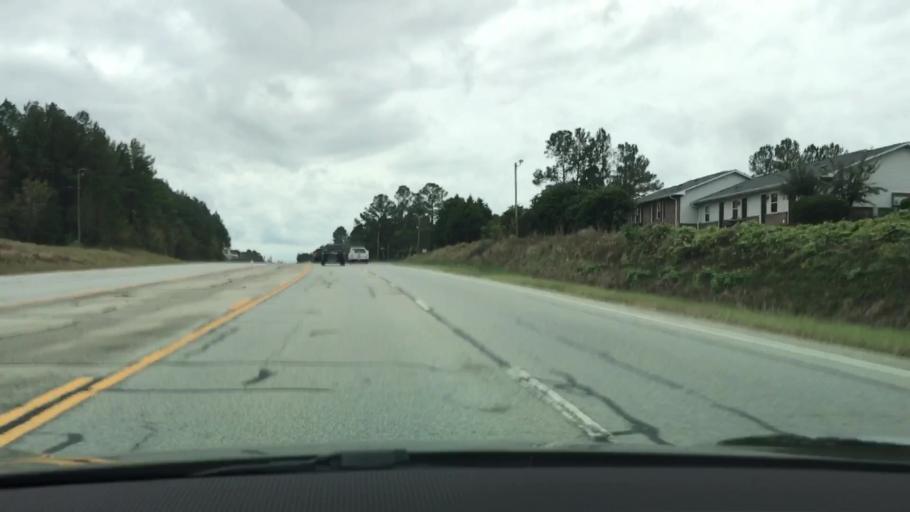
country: US
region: Georgia
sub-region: Jefferson County
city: Wadley
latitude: 32.8748
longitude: -82.3961
